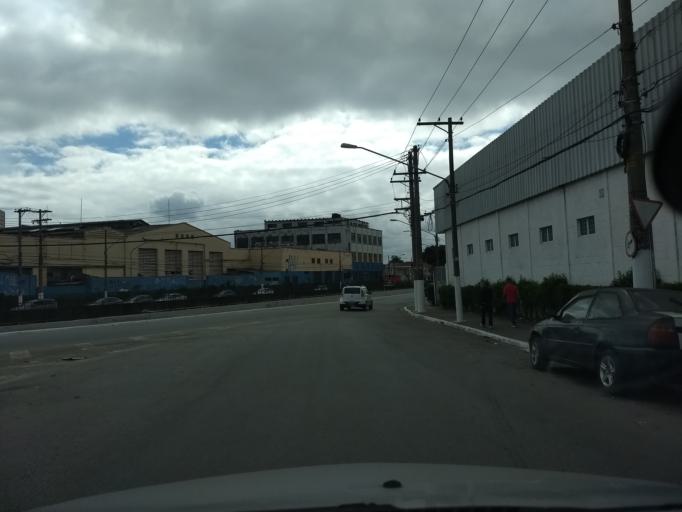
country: BR
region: Sao Paulo
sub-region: Sao Paulo
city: Sao Paulo
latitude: -23.5767
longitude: -46.6087
